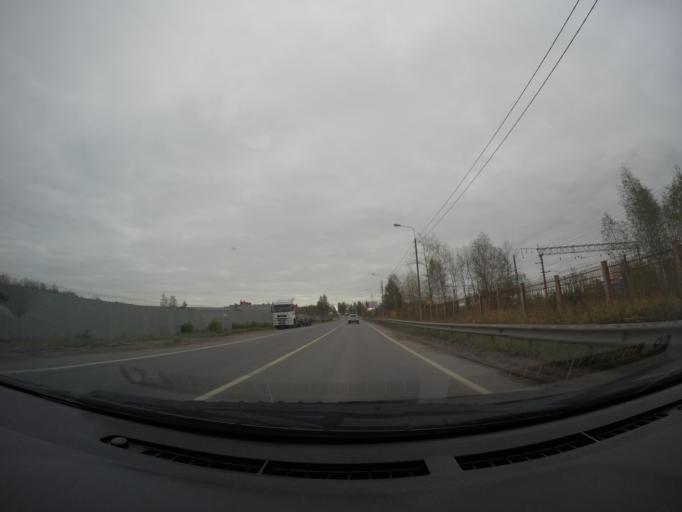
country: RU
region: Moskovskaya
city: Elektrougli
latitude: 55.7266
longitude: 38.2158
